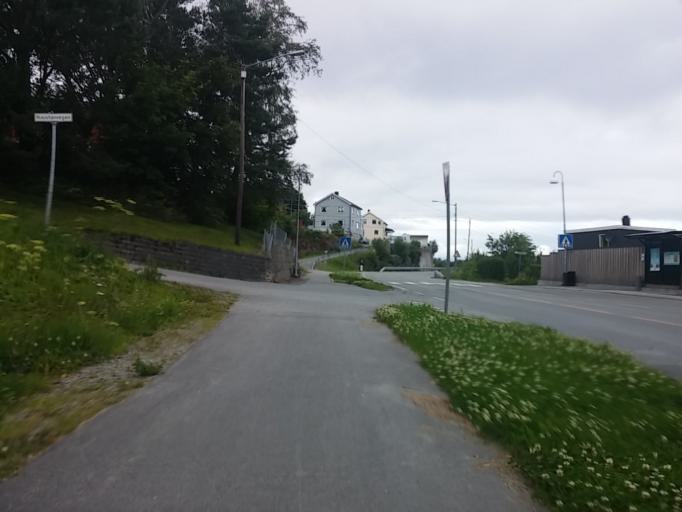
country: NO
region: Sor-Trondelag
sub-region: Malvik
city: Malvik
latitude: 63.4398
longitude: 10.6534
